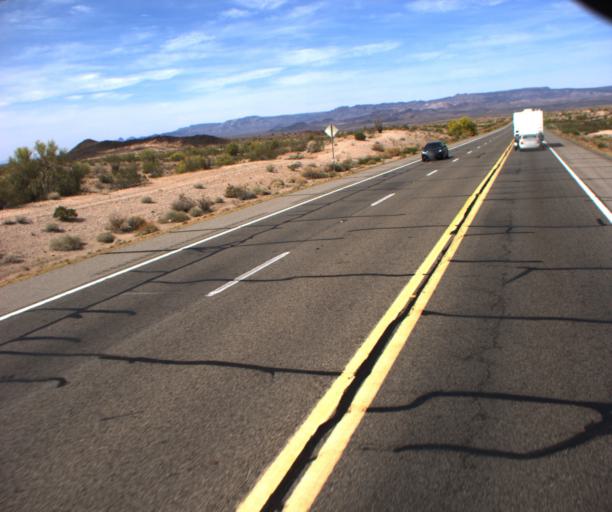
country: US
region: Arizona
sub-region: Mohave County
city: Desert Hills
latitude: 34.6719
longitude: -114.3100
